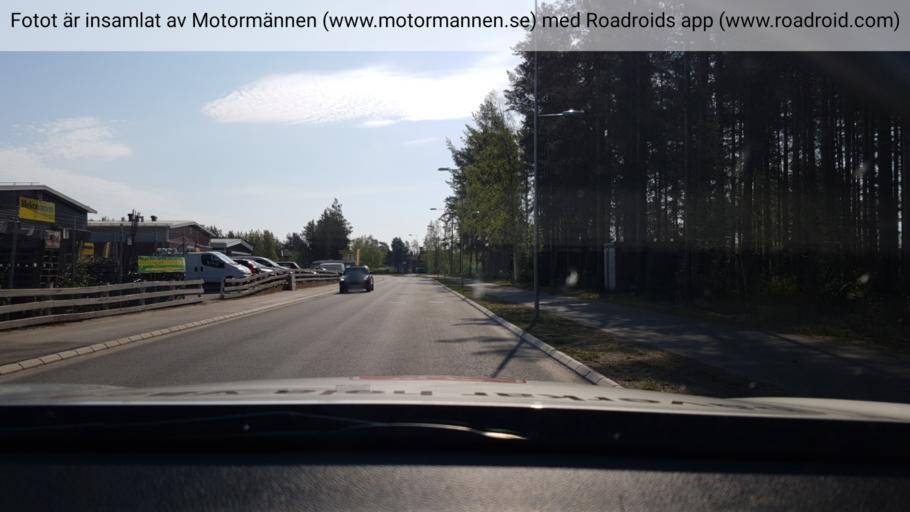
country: SE
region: Vaesterbotten
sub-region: Umea Kommun
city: Roback
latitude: 63.8397
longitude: 20.1961
